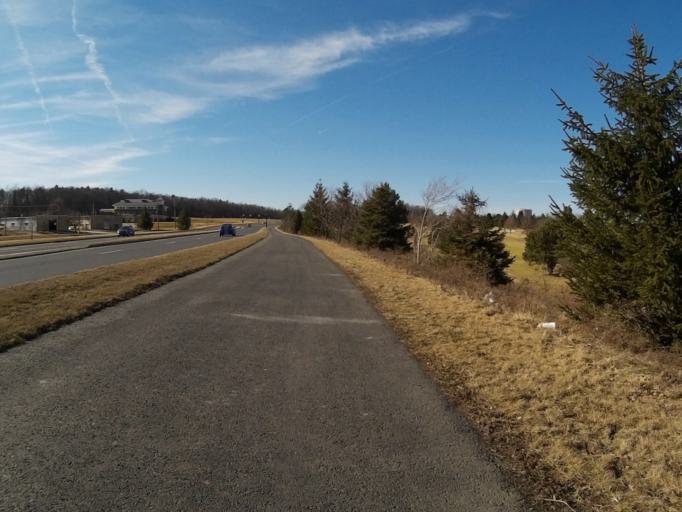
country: US
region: Pennsylvania
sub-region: Centre County
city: State College
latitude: 40.7817
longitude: -77.8826
